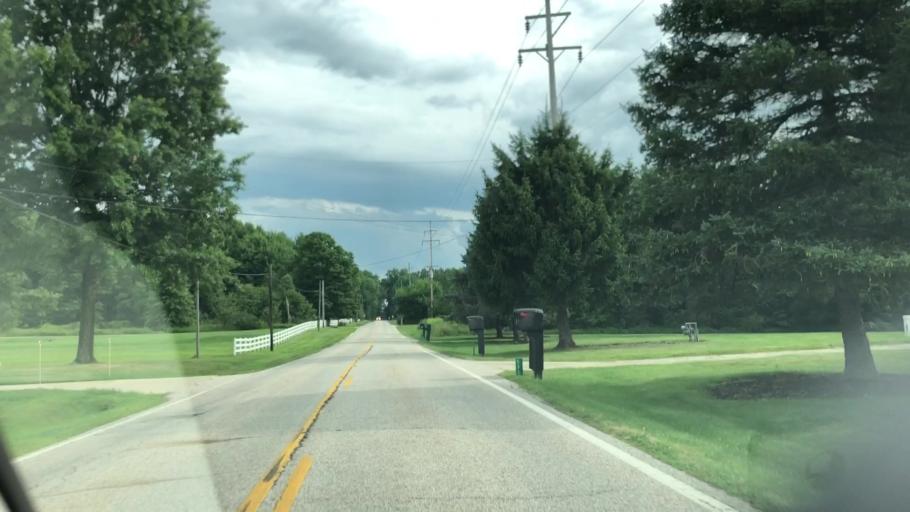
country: US
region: Ohio
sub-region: Summit County
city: Montrose-Ghent
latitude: 41.1308
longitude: -81.7158
